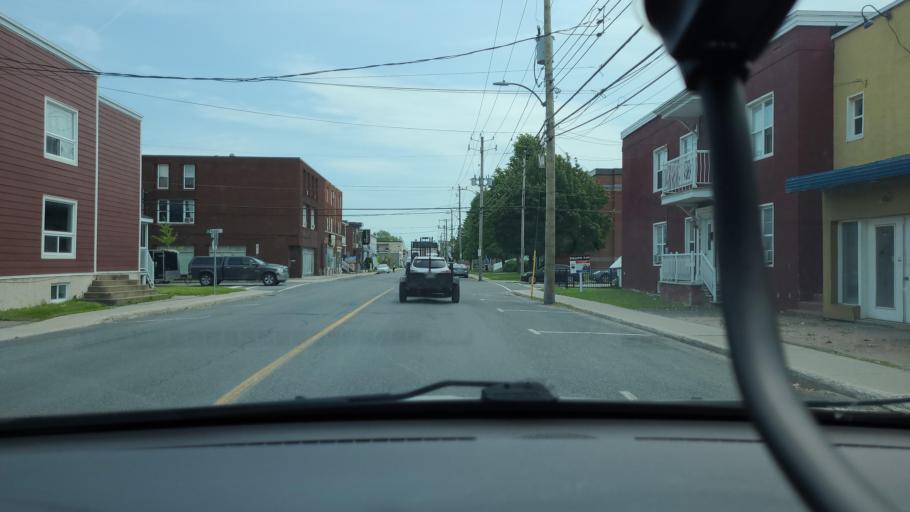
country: CA
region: Quebec
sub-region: Monteregie
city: Saint-Hyacinthe
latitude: 45.6302
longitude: -72.9551
